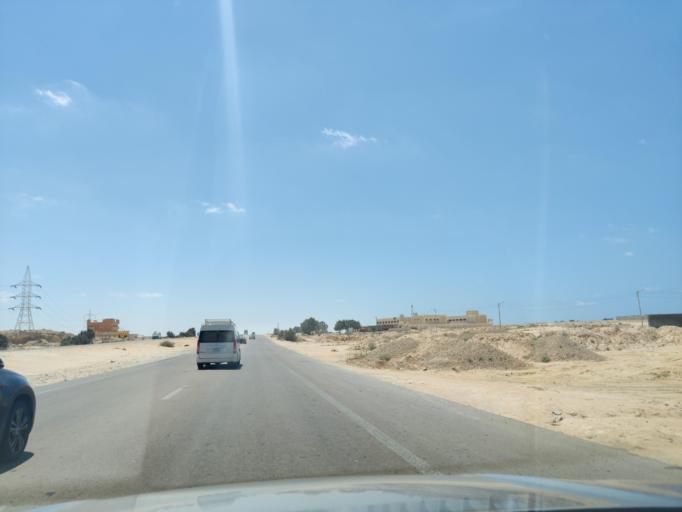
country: EG
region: Muhafazat Matruh
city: Al `Alamayn
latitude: 31.0701
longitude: 28.1520
